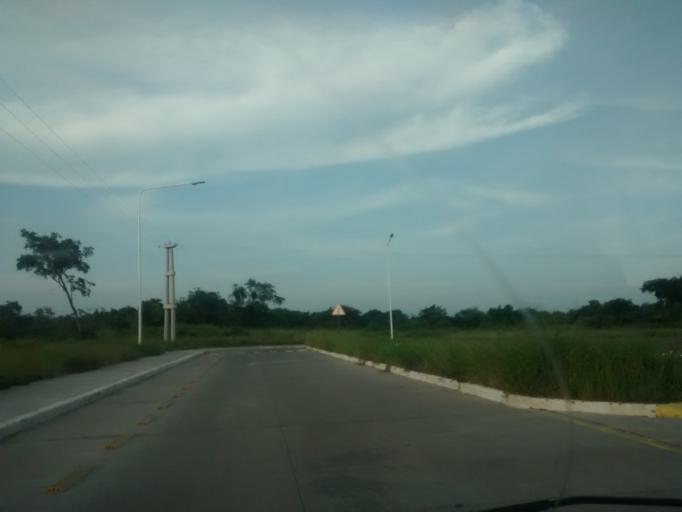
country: AR
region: Chaco
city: Resistencia
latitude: -27.4317
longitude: -58.9727
